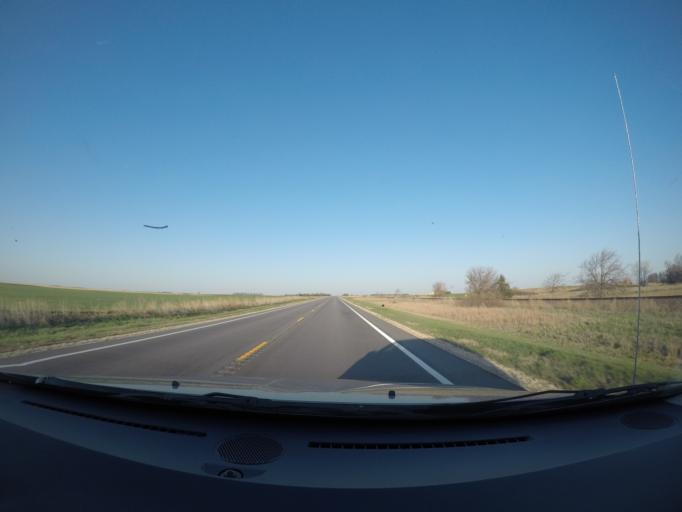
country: US
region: Kansas
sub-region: Stafford County
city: Stafford
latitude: 37.8019
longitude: -98.4520
